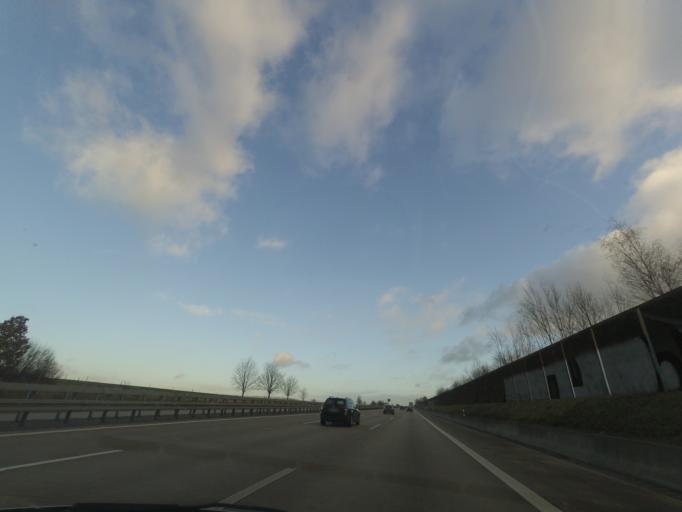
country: DE
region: Saxony
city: Wilsdruff
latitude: 51.0606
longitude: 13.5350
